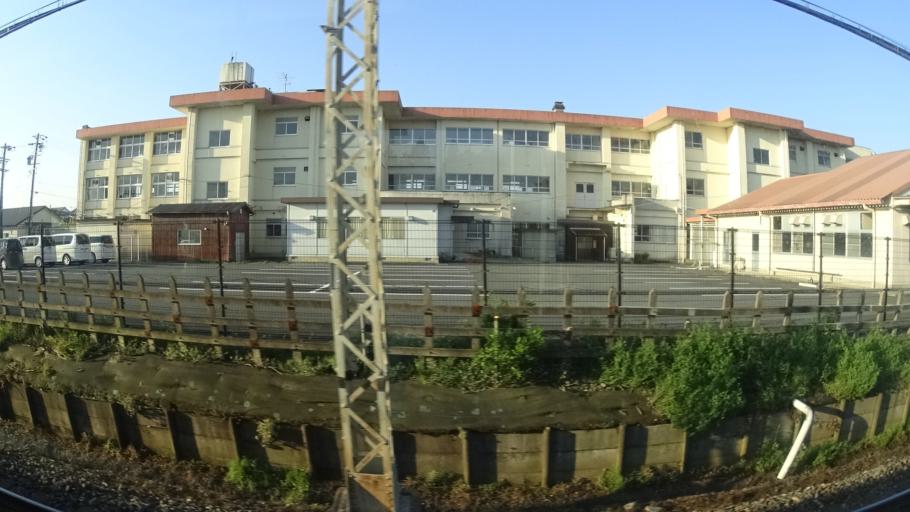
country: JP
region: Mie
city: Ise
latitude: 34.5381
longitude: 136.6115
